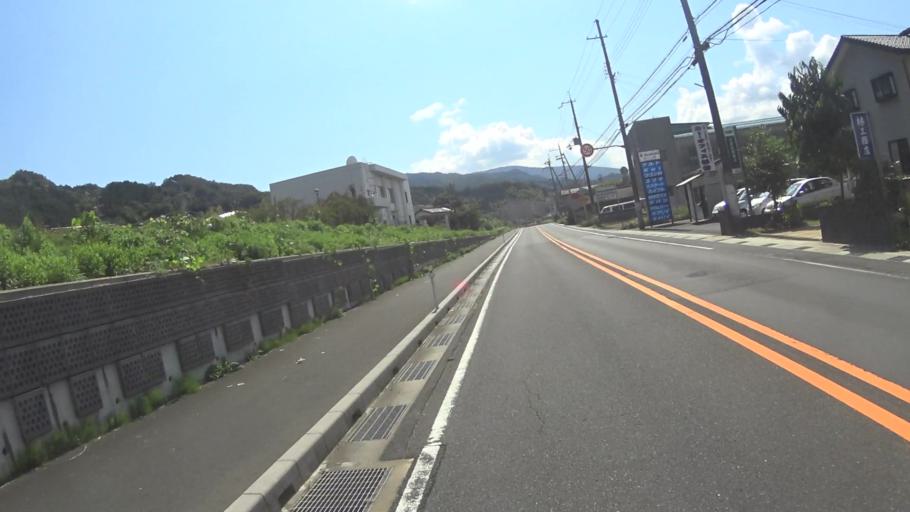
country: JP
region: Kyoto
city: Miyazu
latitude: 35.5461
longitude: 135.2109
